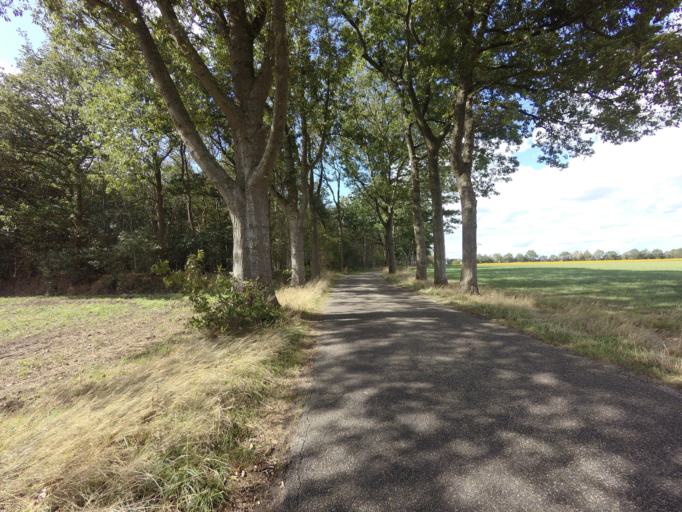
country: NL
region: Friesland
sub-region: Gemeente Heerenveen
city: Jubbega
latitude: 52.9614
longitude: 6.2035
